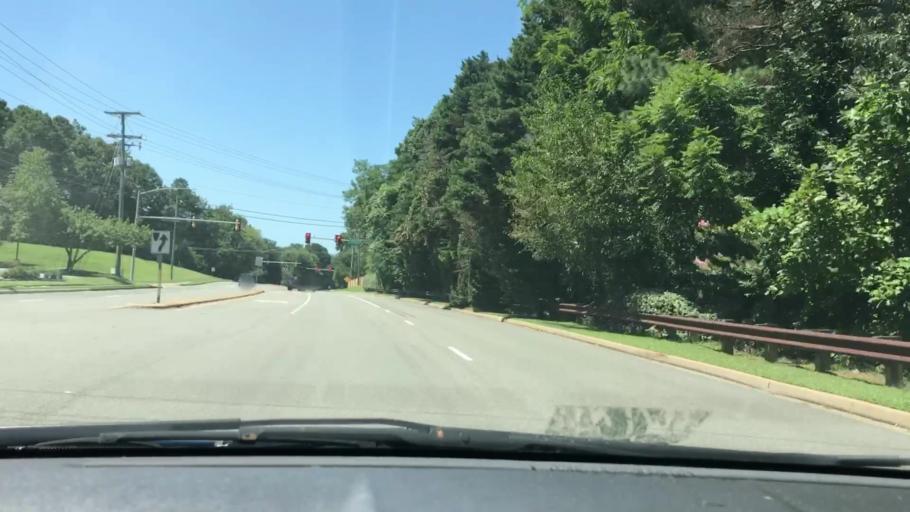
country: US
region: Virginia
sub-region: Henrico County
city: Tuckahoe
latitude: 37.6073
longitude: -77.5937
